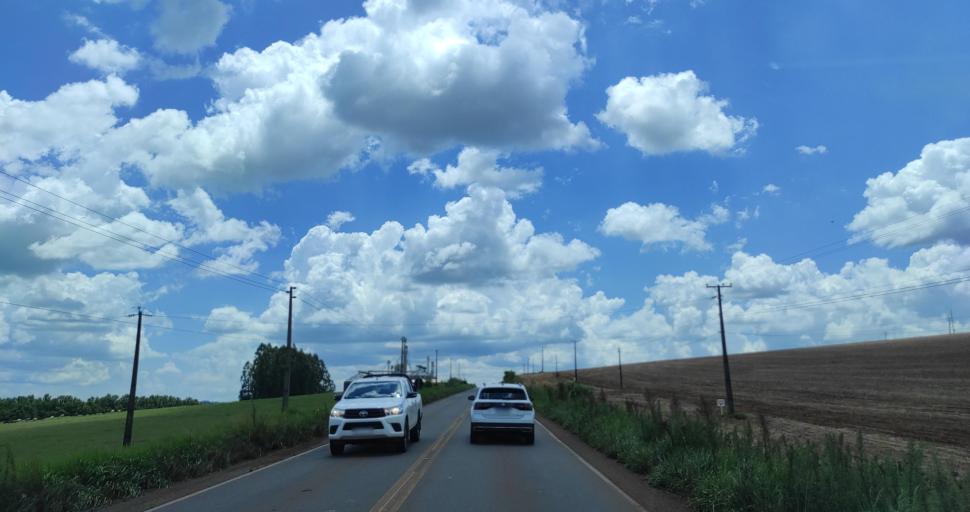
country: BR
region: Santa Catarina
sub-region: Xanxere
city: Xanxere
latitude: -26.7667
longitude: -52.4051
